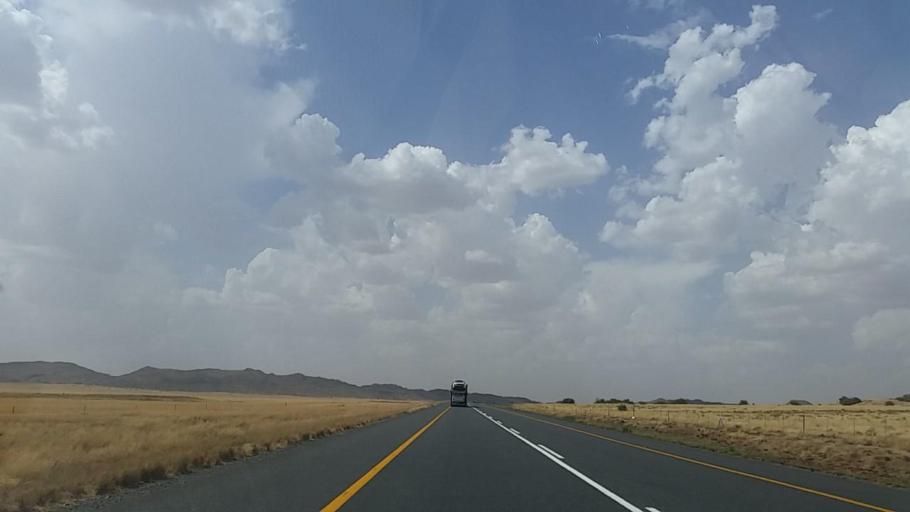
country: ZA
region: Orange Free State
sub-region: Xhariep District Municipality
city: Trompsburg
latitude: -30.4285
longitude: 25.6343
